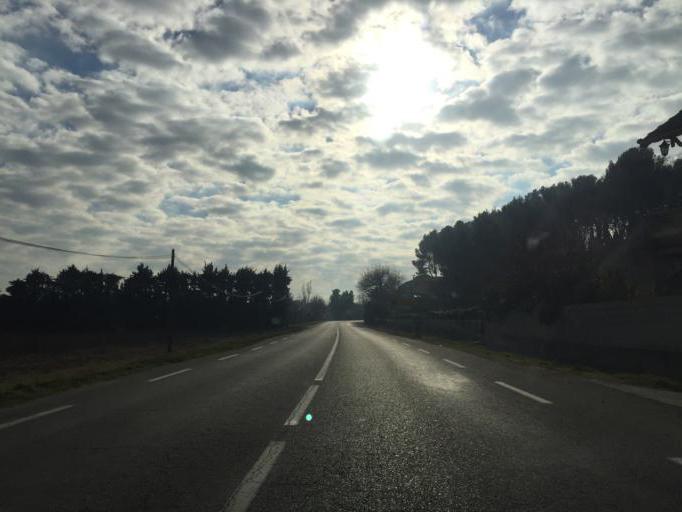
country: FR
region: Provence-Alpes-Cote d'Azur
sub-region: Departement du Vaucluse
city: Sarrians
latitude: 44.0906
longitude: 4.9720
